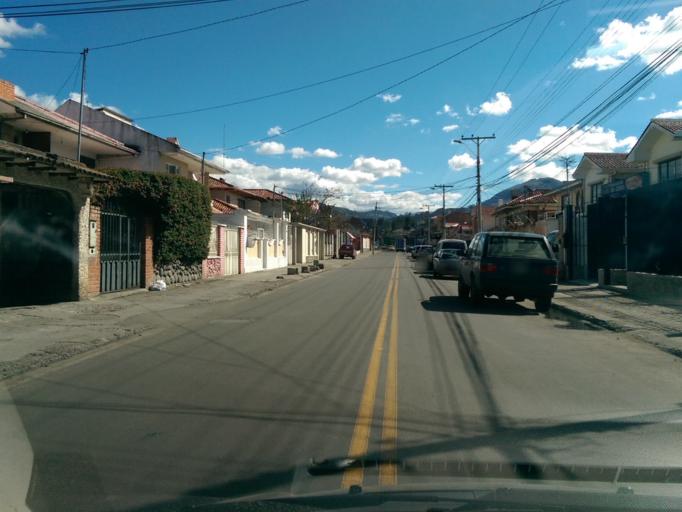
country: EC
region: Azuay
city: Cuenca
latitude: -2.9016
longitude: -79.0186
